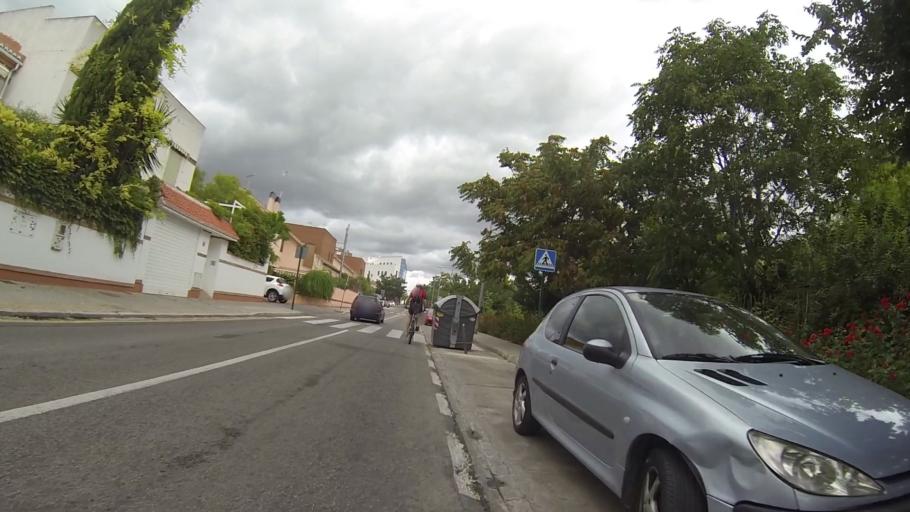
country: ES
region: Andalusia
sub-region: Provincia de Granada
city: Granada
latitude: 37.1940
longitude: -3.6207
